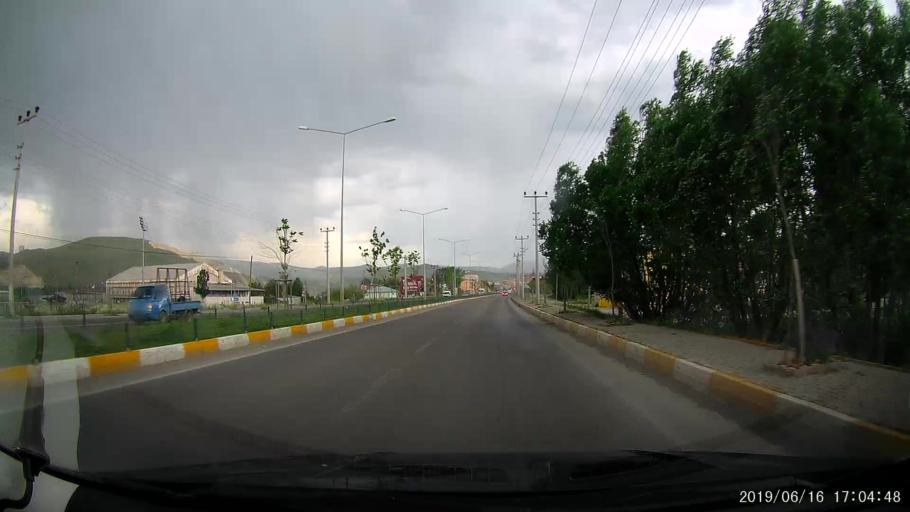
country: TR
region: Erzurum
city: Askale
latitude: 39.9238
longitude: 40.7046
